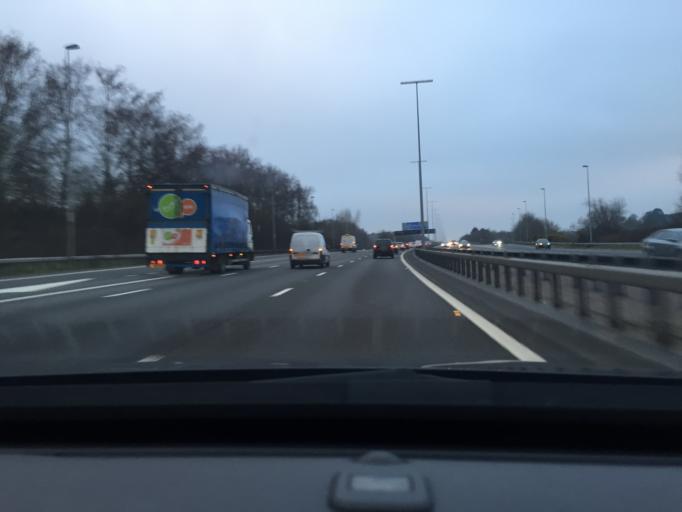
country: GB
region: England
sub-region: Hampshire
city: Bursledon
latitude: 50.8944
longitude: -1.3097
